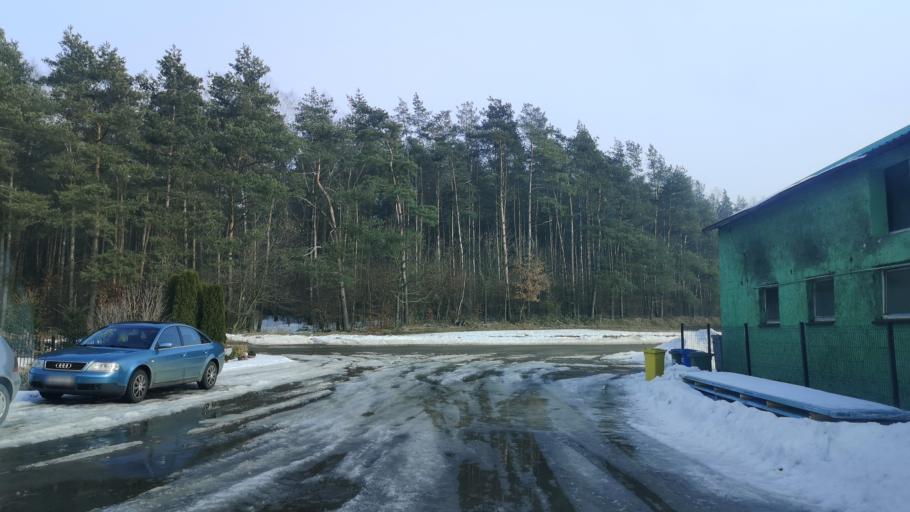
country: PL
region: Warmian-Masurian Voivodeship
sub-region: Powiat nowomiejski
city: Biskupiec
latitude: 53.5454
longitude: 19.3576
